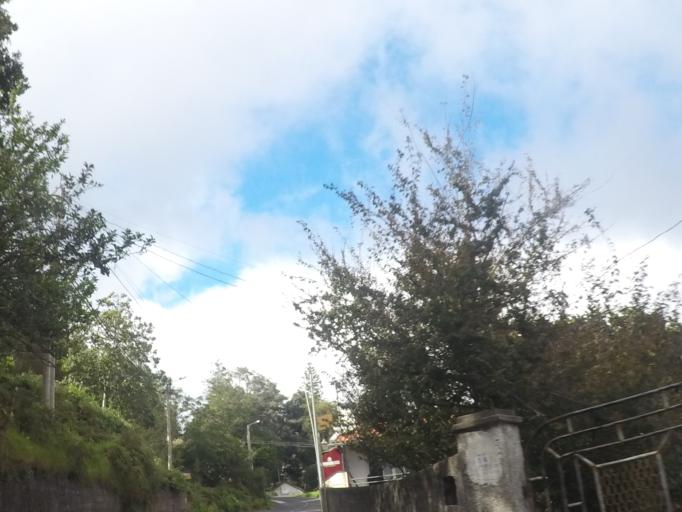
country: PT
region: Madeira
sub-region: Santa Cruz
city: Camacha
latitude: 32.6780
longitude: -16.8522
